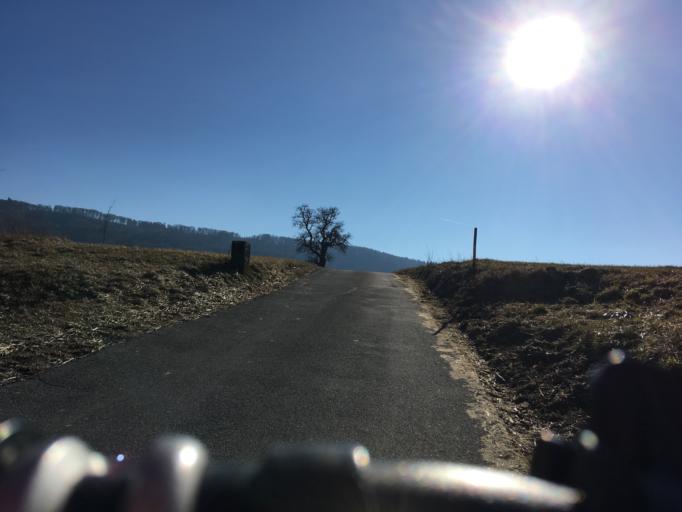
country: DE
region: Baden-Wuerttemberg
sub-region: Freiburg Region
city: Gottmadingen
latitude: 47.7186
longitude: 8.7697
